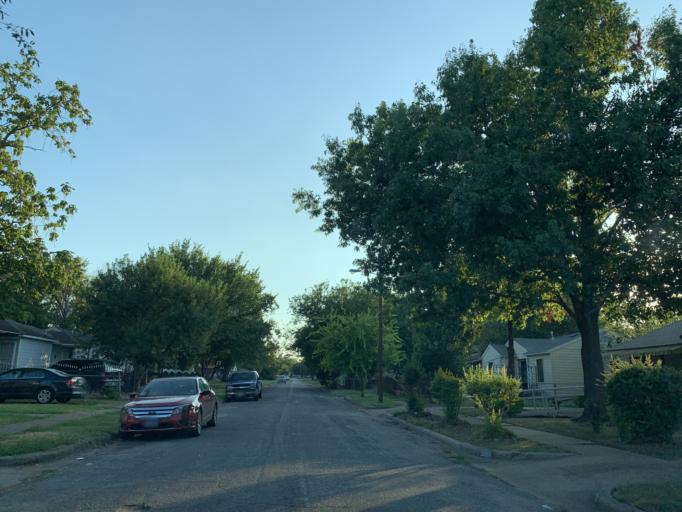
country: US
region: Texas
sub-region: Dallas County
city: Dallas
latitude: 32.7086
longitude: -96.7842
